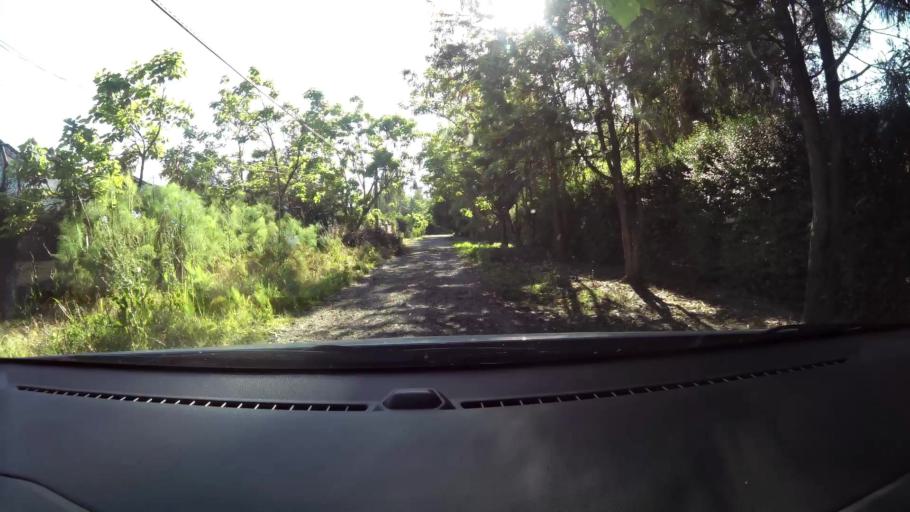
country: CL
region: Santiago Metropolitan
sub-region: Provincia de Maipo
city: San Bernardo
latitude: -33.6438
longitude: -70.6867
